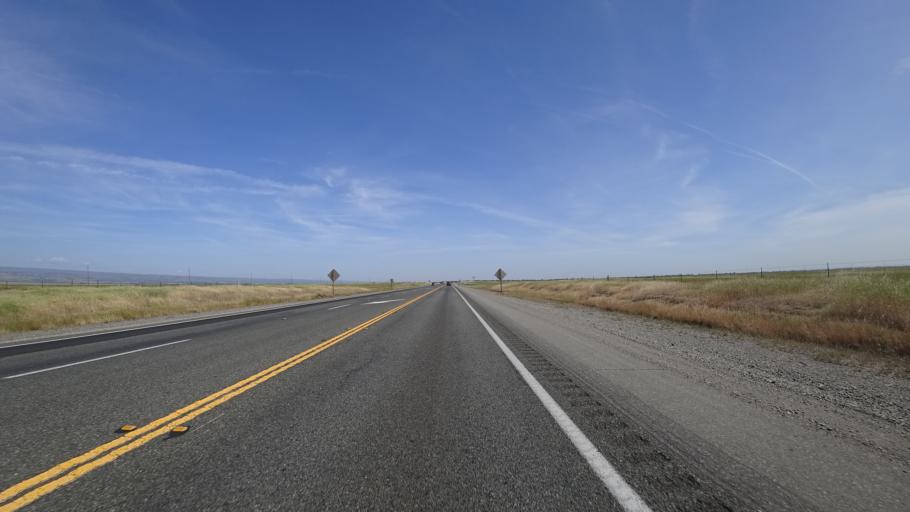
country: US
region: California
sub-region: Tehama County
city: Los Molinos
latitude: 39.9097
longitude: -122.0077
